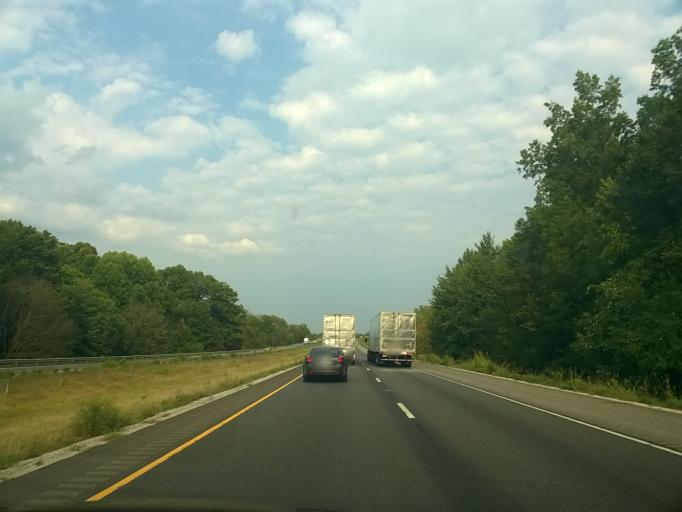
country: US
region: Indiana
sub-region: Clay County
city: Brazil
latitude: 39.4684
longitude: -87.0397
